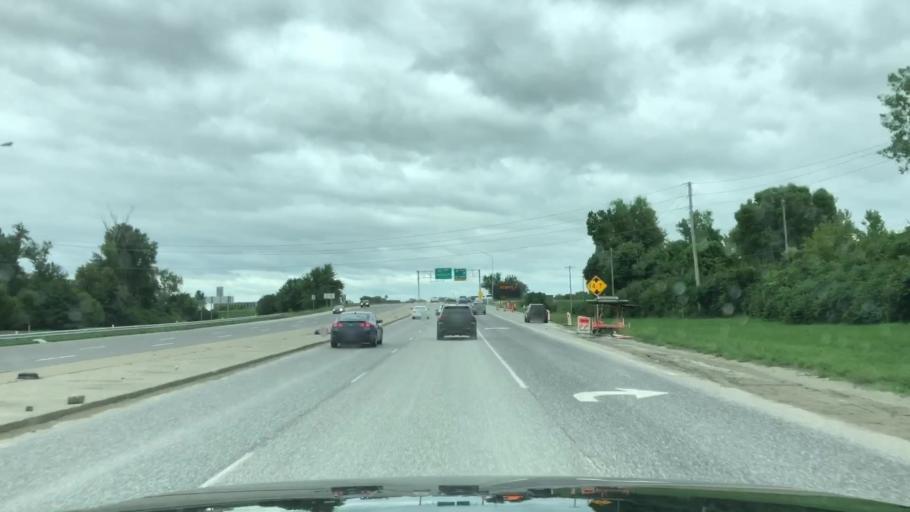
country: US
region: Missouri
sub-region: Saint Charles County
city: Saint Charles
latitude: 38.7504
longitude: -90.4618
